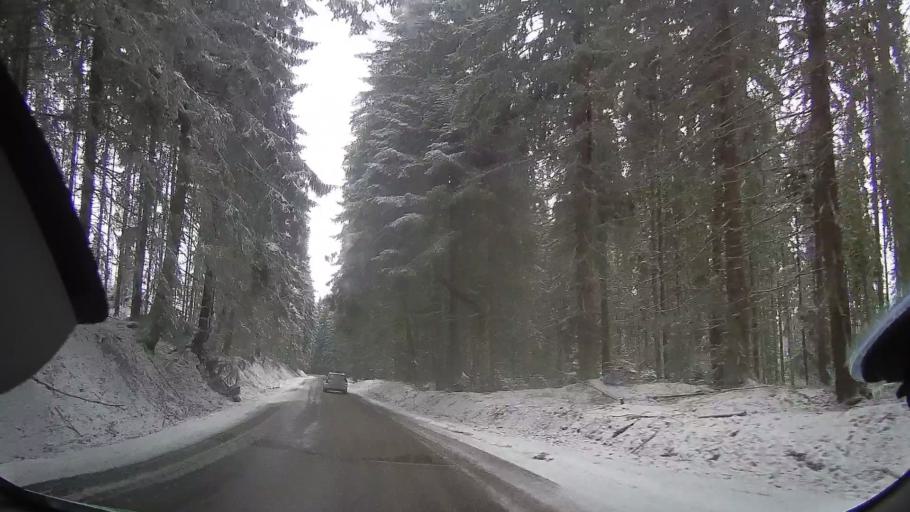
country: RO
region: Cluj
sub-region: Comuna Belis
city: Belis
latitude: 46.6494
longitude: 23.0459
